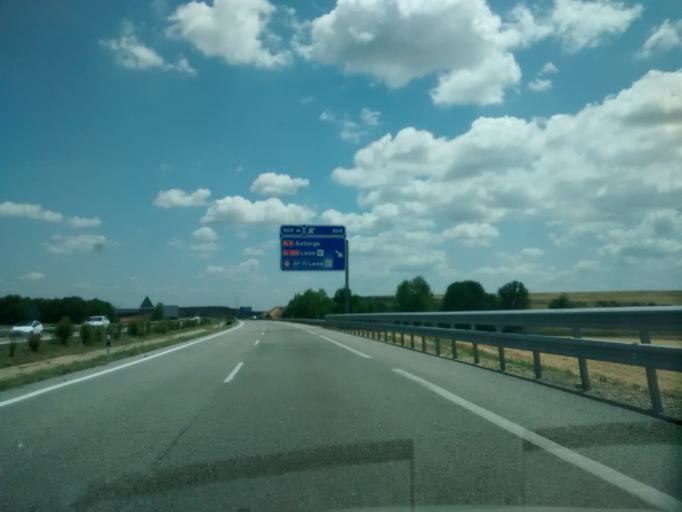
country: ES
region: Castille and Leon
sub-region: Provincia de Leon
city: Astorga
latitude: 42.4395
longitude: -6.0640
